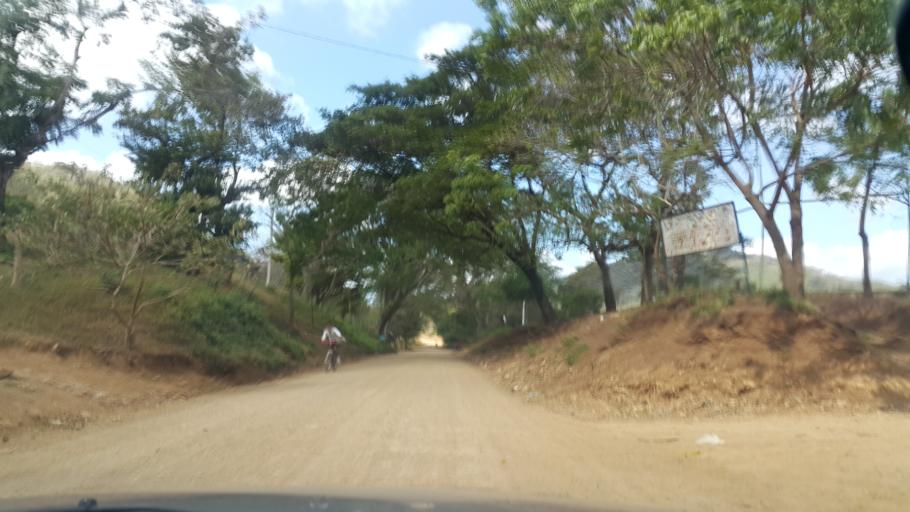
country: NI
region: Rivas
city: San Juan del Sur
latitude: 11.3016
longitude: -85.8723
